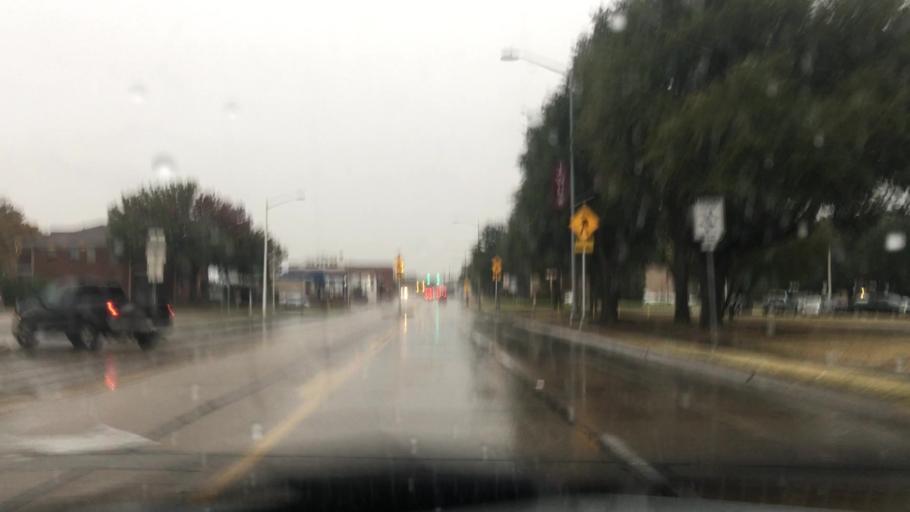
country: US
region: Texas
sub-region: Denton County
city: Denton
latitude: 33.2166
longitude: -97.1294
